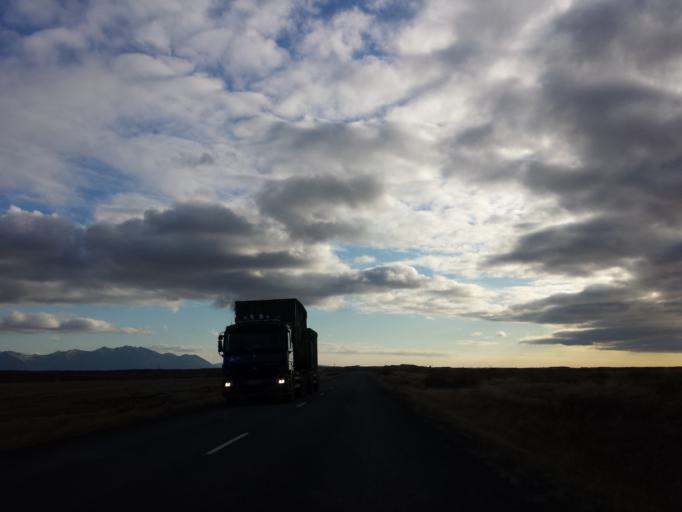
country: IS
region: West
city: Borgarnes
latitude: 64.6613
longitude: -22.0695
